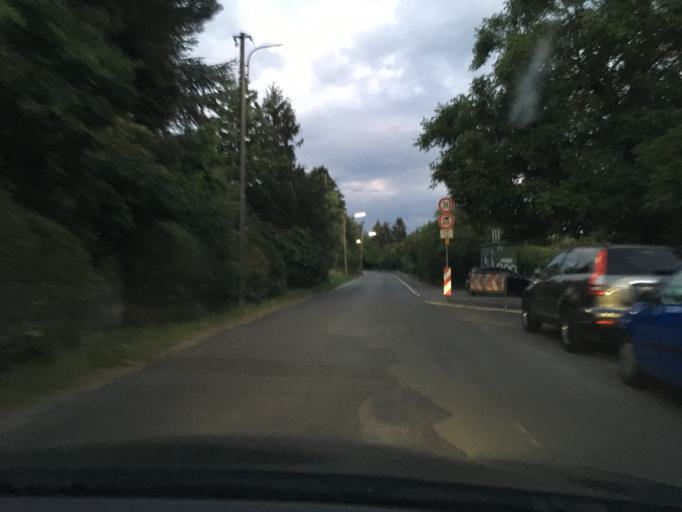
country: DE
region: Hesse
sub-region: Regierungsbezirk Darmstadt
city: Bad Vilbel
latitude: 50.1411
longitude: 8.7267
